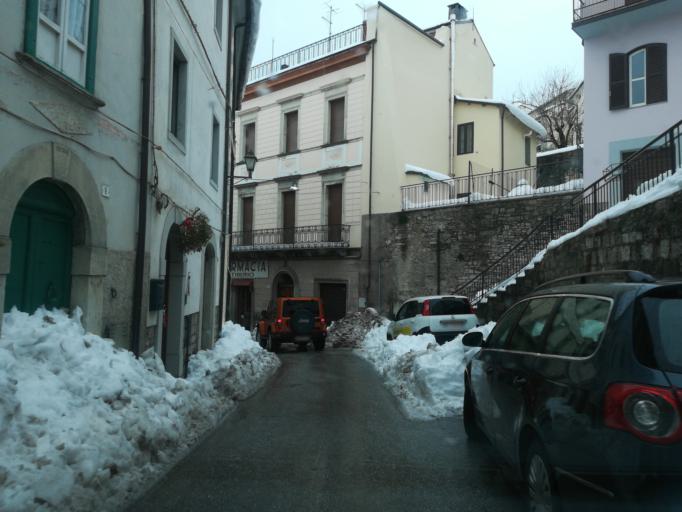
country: IT
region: Molise
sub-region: Provincia di Isernia
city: Agnone
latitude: 41.8069
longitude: 14.3671
